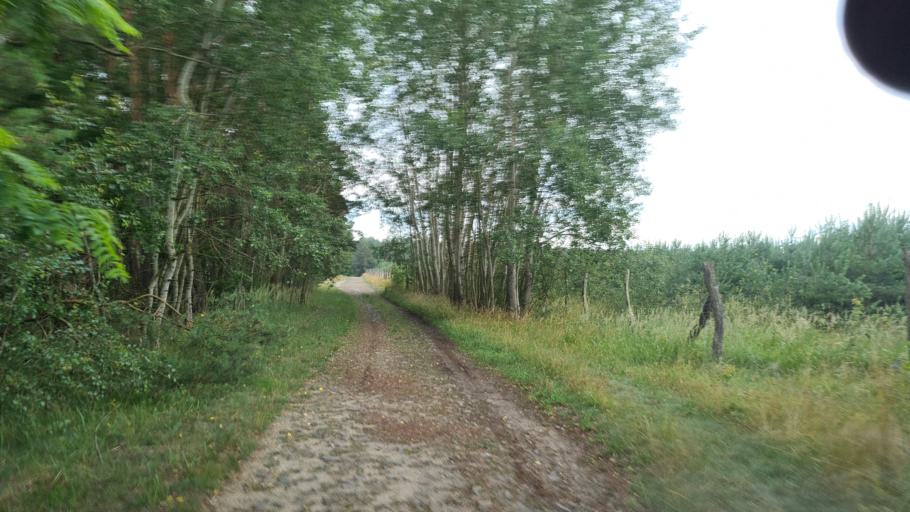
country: DE
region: Brandenburg
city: Sonnewalde
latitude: 51.7308
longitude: 13.6982
